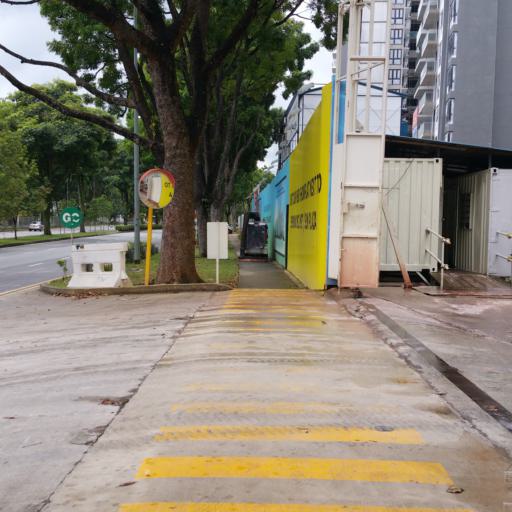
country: MY
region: Johor
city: Kampung Pasir Gudang Baru
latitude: 1.4177
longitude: 103.8460
